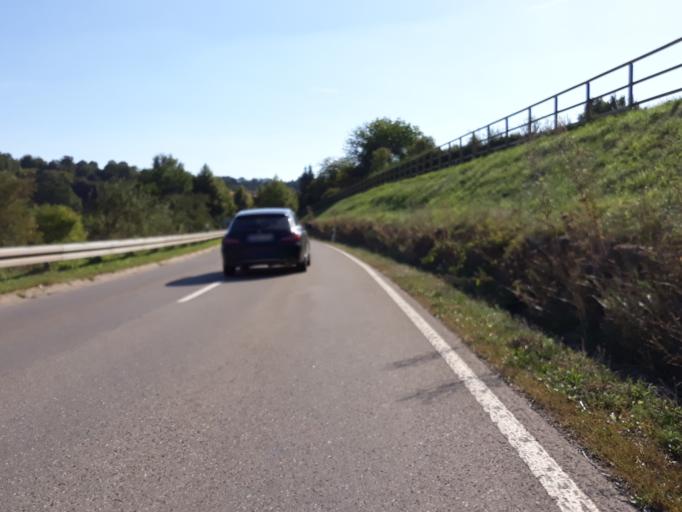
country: DE
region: Baden-Wuerttemberg
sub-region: Karlsruhe Region
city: Gechingen
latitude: 48.6983
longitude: 8.8377
